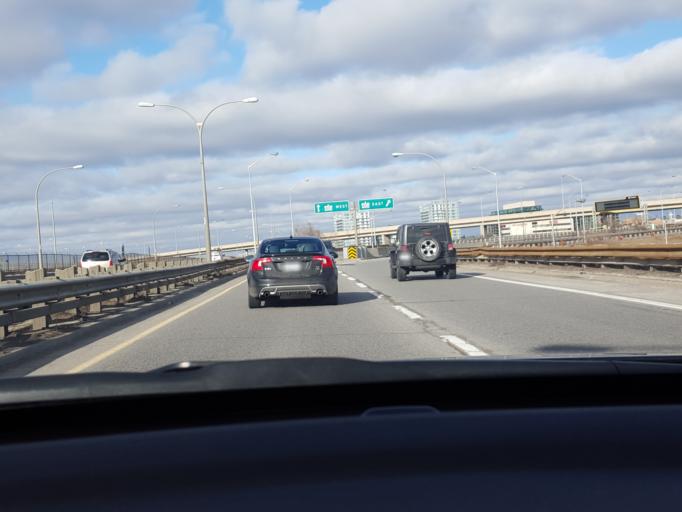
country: CA
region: Ontario
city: Toronto
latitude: 43.7265
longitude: -79.4478
